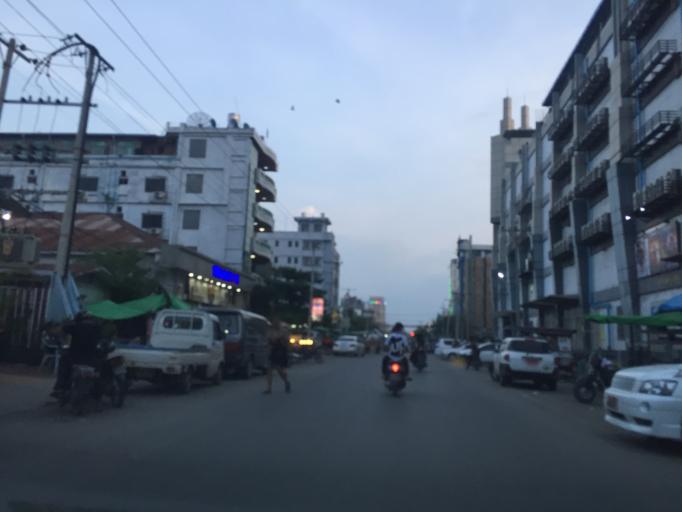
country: MM
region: Mandalay
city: Mandalay
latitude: 21.9717
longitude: 96.0882
